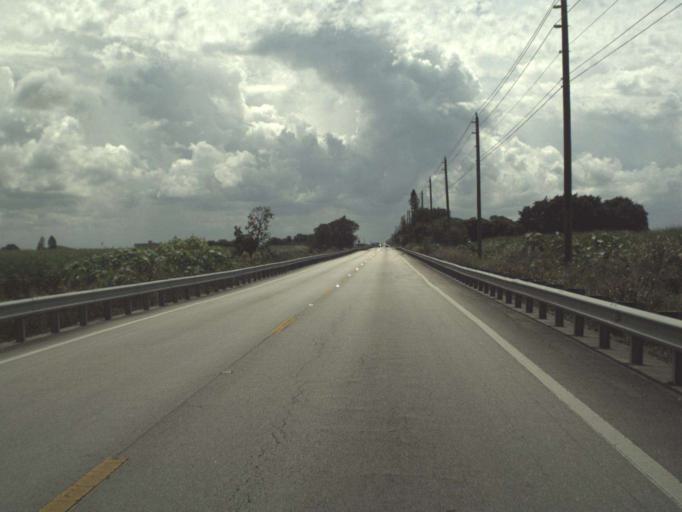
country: US
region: Florida
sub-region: Palm Beach County
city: Pahokee
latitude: 26.7967
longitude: -80.6534
